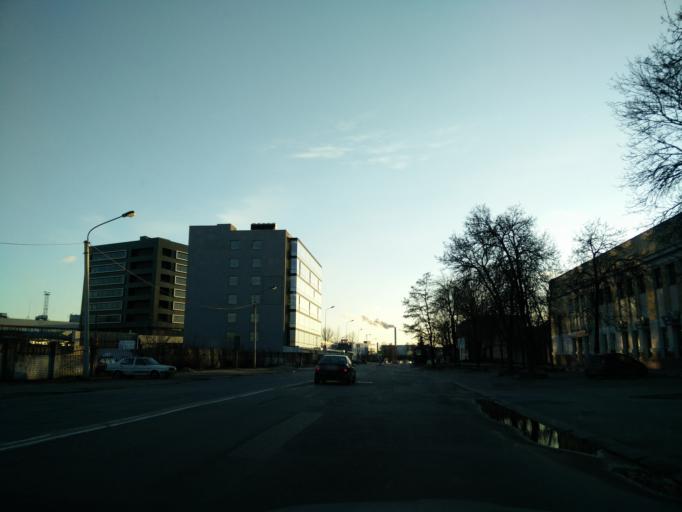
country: LT
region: Vilnius County
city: Vilkpede
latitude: 54.6688
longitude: 25.2564
